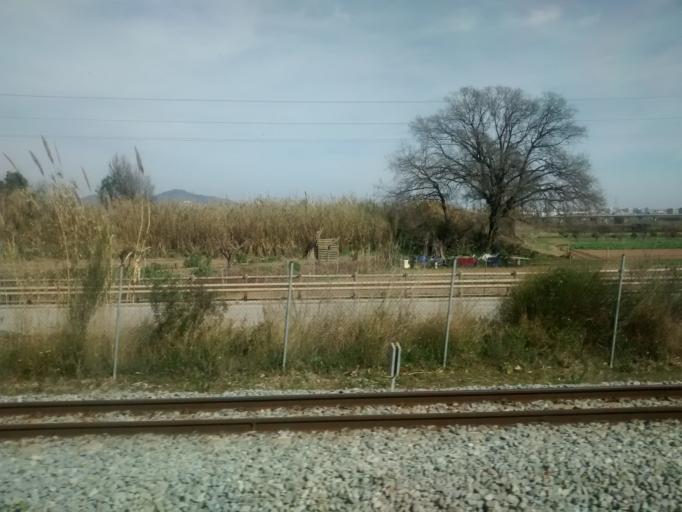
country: ES
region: Catalonia
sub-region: Provincia de Barcelona
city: Sant Boi de Llobregat
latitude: 41.3606
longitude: 2.0333
